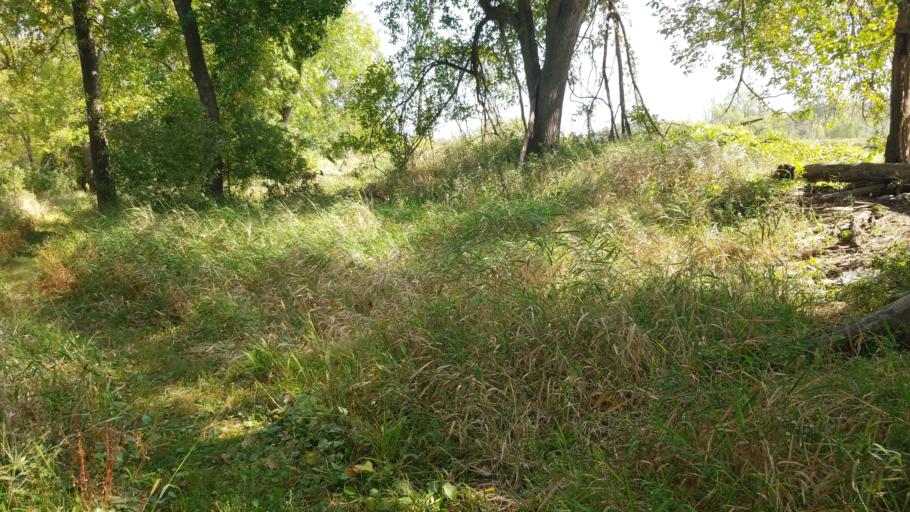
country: US
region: Nebraska
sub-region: Sarpy County
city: Bellevue
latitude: 41.1707
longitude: -95.8898
